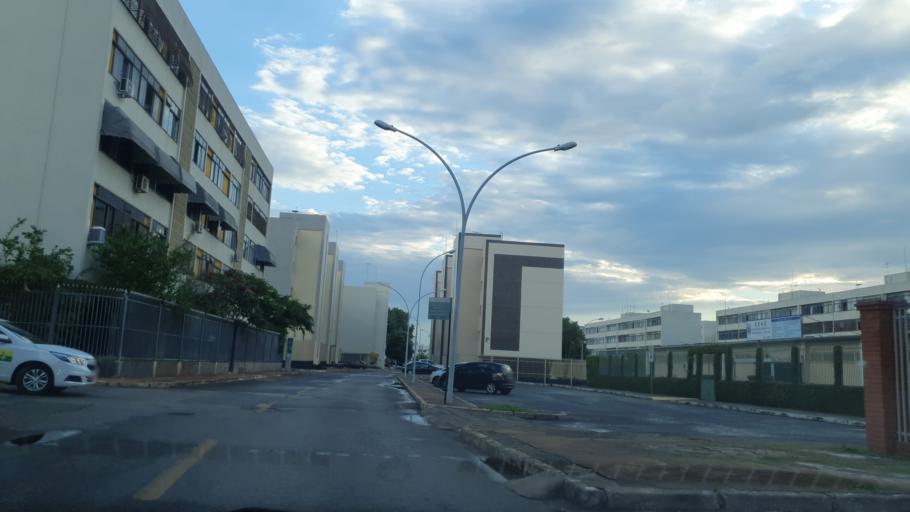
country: BR
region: Federal District
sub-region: Brasilia
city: Brasilia
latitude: -15.7968
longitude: -47.9372
